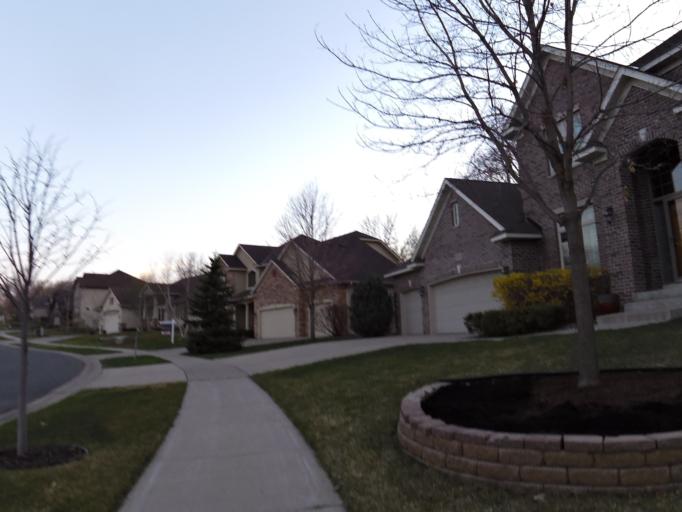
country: US
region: Minnesota
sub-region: Scott County
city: Prior Lake
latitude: 44.7313
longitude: -93.4439
